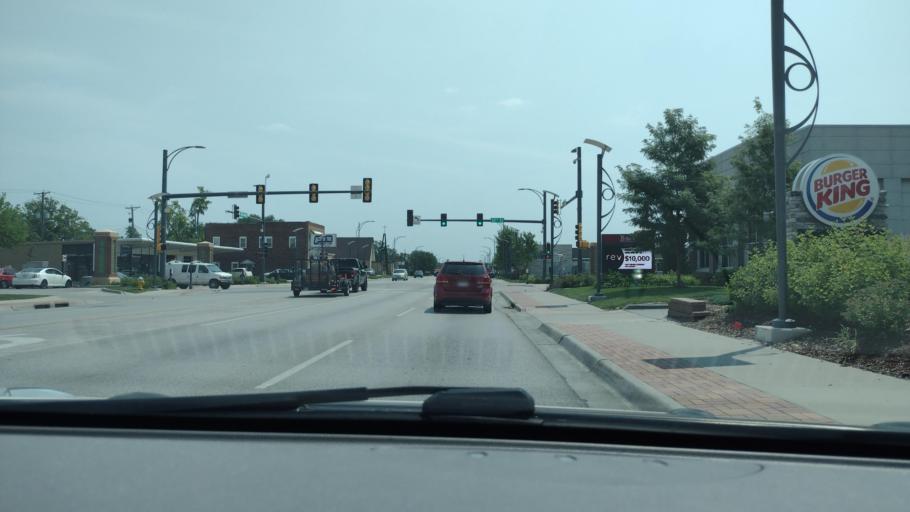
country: US
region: Iowa
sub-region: Pottawattamie County
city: Carter Lake
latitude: 41.2619
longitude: -95.8970
